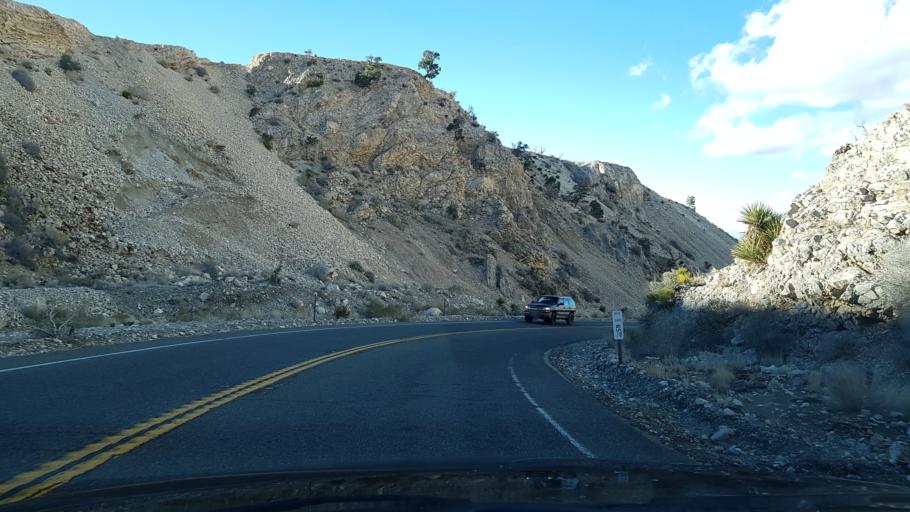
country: US
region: California
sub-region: San Bernardino County
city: Big Bear City
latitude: 34.3477
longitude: -116.8456
